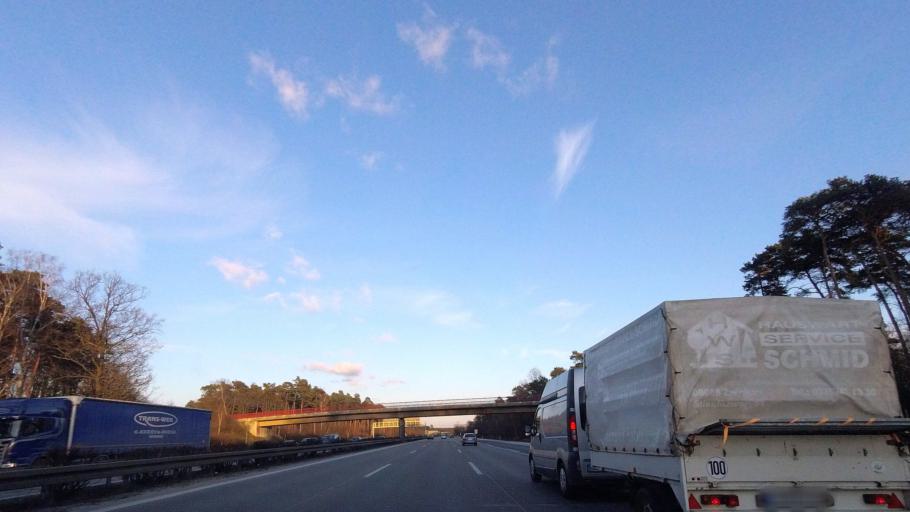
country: DE
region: Brandenburg
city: Schulzendorf
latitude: 52.3200
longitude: 13.5685
